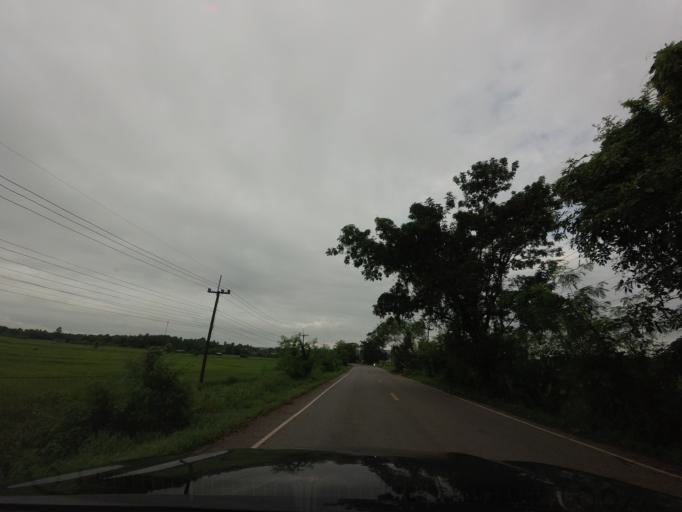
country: TH
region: Changwat Udon Thani
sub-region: Amphoe Ban Phue
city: Ban Phue
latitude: 17.7185
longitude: 102.3978
